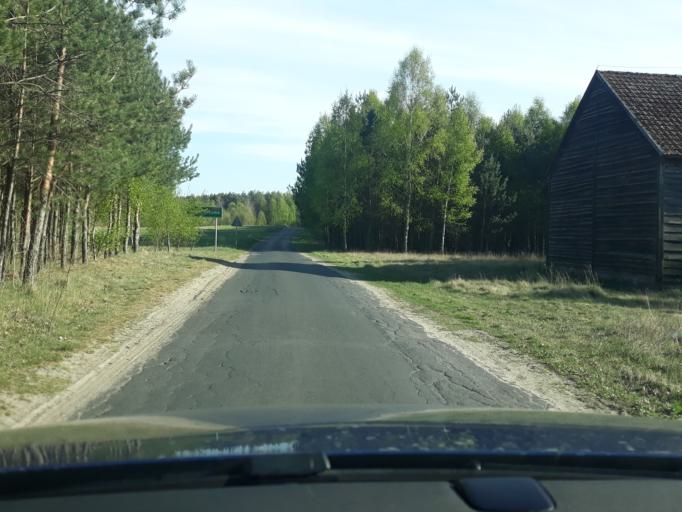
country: PL
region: Pomeranian Voivodeship
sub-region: Powiat czluchowski
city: Przechlewo
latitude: 53.8699
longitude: 17.3331
